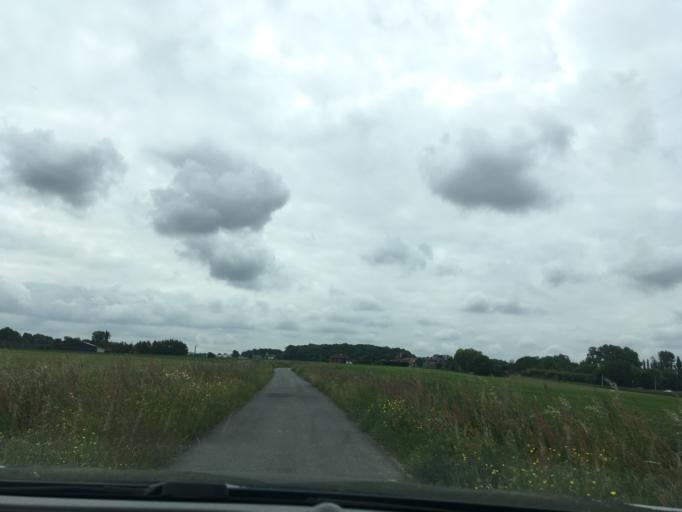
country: BE
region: Wallonia
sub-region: Province du Hainaut
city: Mouscron
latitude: 50.7674
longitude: 3.1883
